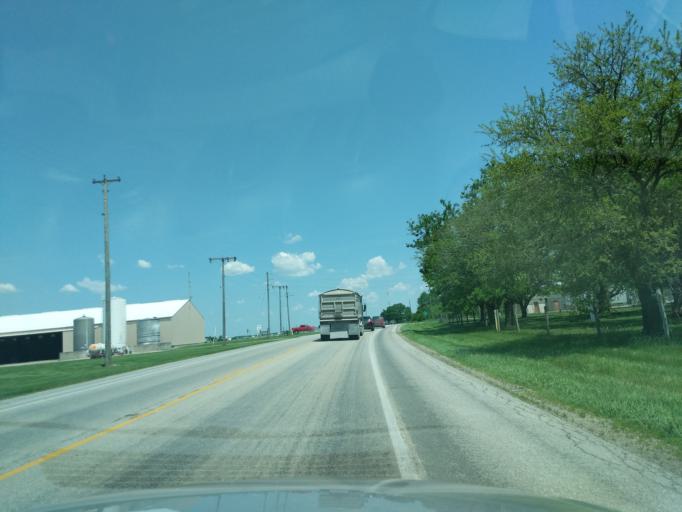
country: US
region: Indiana
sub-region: LaGrange County
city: Topeka
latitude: 41.5233
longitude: -85.5780
